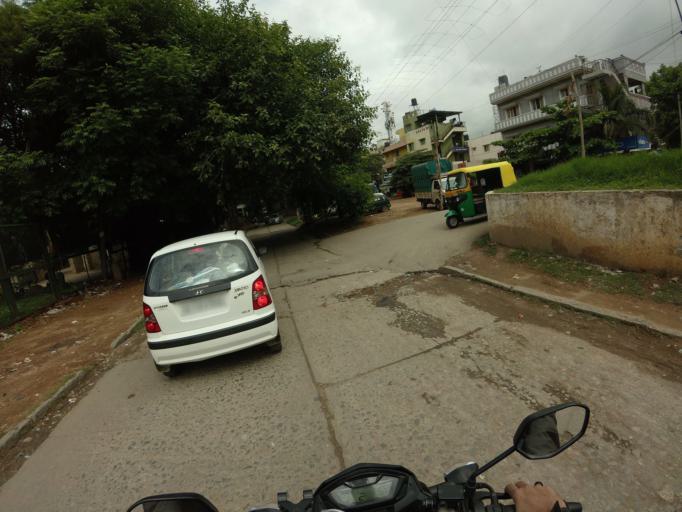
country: IN
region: Karnataka
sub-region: Bangalore Urban
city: Bangalore
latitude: 12.9715
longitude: 77.6659
